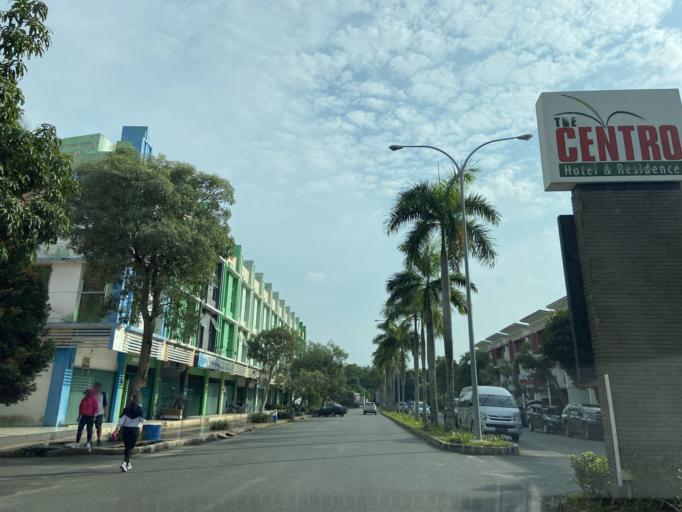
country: SG
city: Singapore
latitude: 1.1016
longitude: 104.0340
